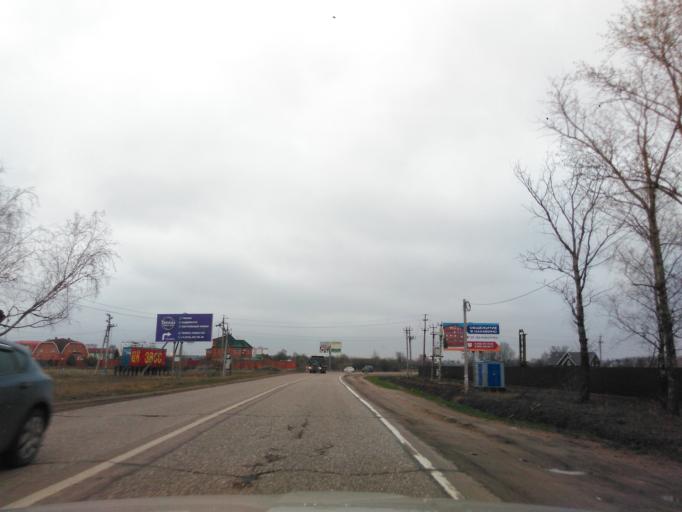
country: RU
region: Moskovskaya
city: Nakhabino
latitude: 55.8281
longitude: 37.1400
